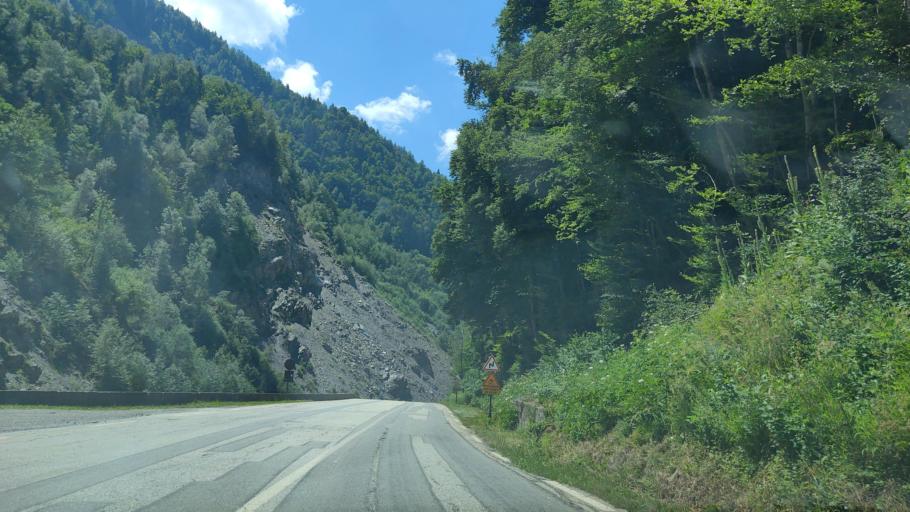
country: FR
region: Rhone-Alpes
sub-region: Departement de la Savoie
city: Ugine
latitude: 45.7584
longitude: 6.4716
